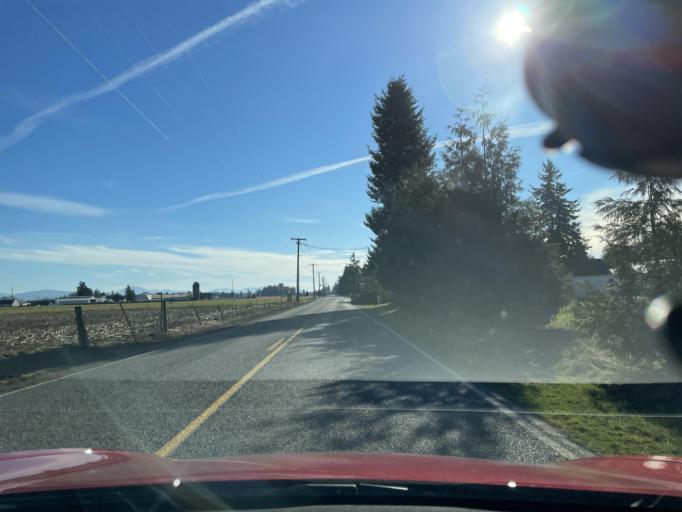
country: US
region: Washington
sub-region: Whatcom County
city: Lynden
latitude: 48.9508
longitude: -122.5073
